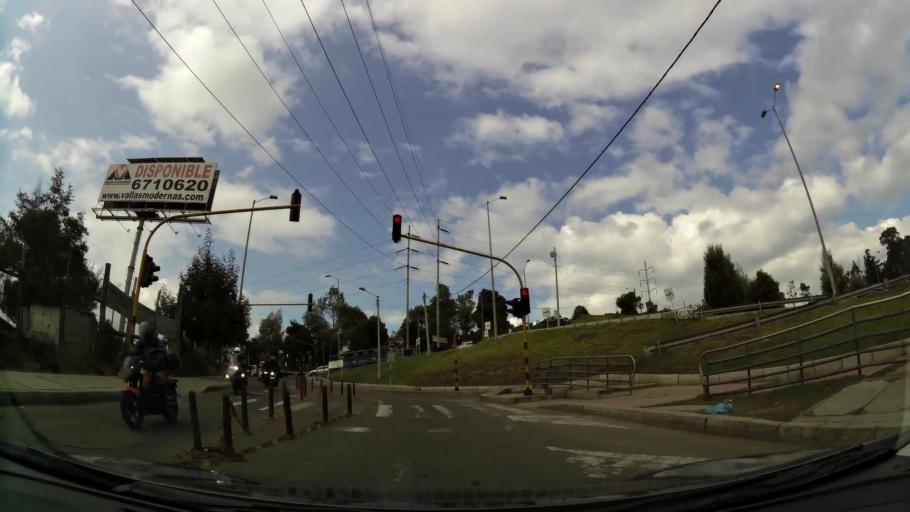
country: CO
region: Cundinamarca
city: Cota
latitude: 4.7585
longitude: -74.0776
